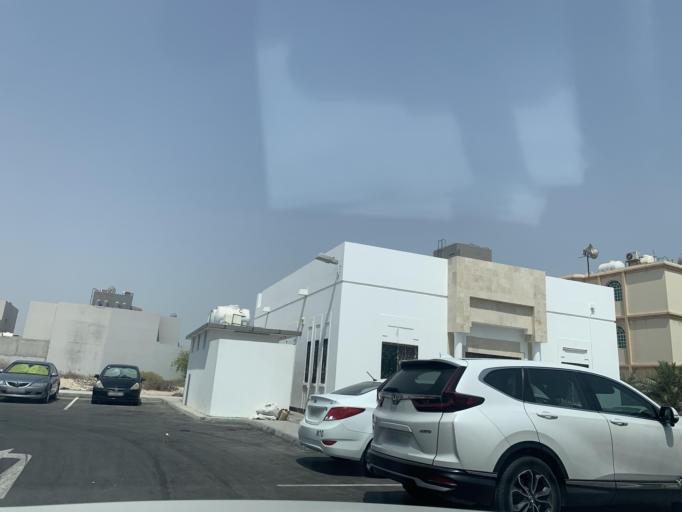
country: BH
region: Manama
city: Jidd Hafs
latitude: 26.2099
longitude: 50.5037
